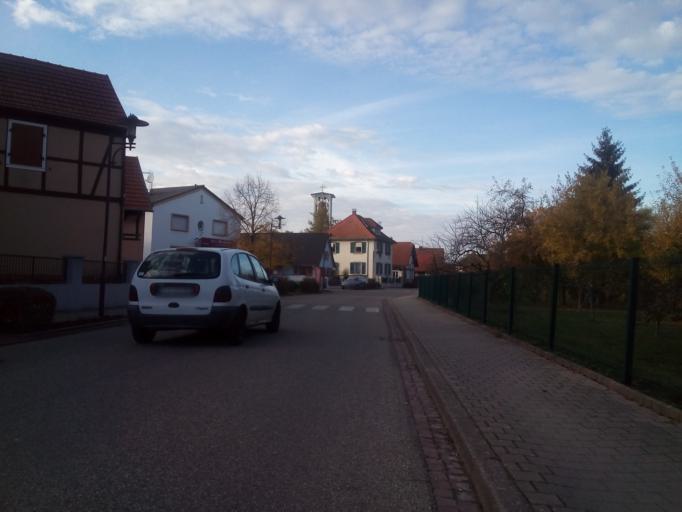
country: FR
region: Alsace
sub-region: Departement du Bas-Rhin
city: Herrlisheim
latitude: 48.7102
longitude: 7.9152
